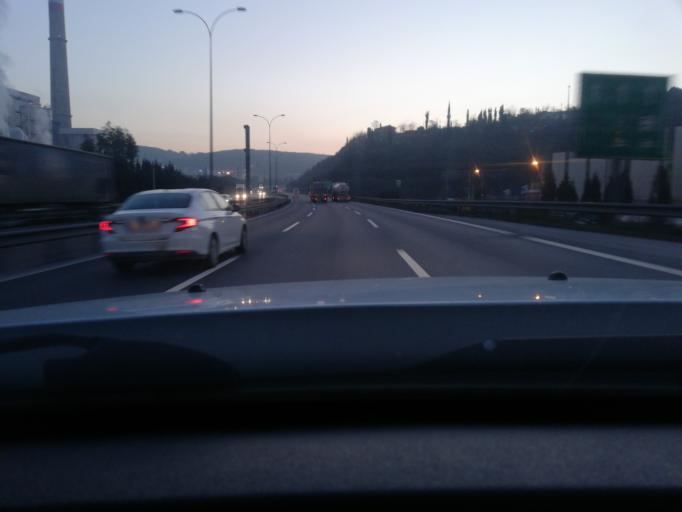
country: TR
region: Kocaeli
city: Tavsancil
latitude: 40.7754
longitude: 29.5347
